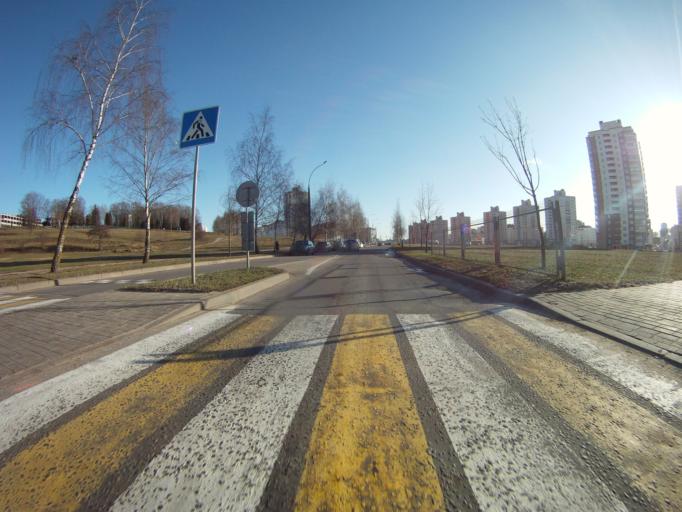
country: BY
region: Minsk
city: Novoye Medvezhino
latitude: 53.8793
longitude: 27.4457
